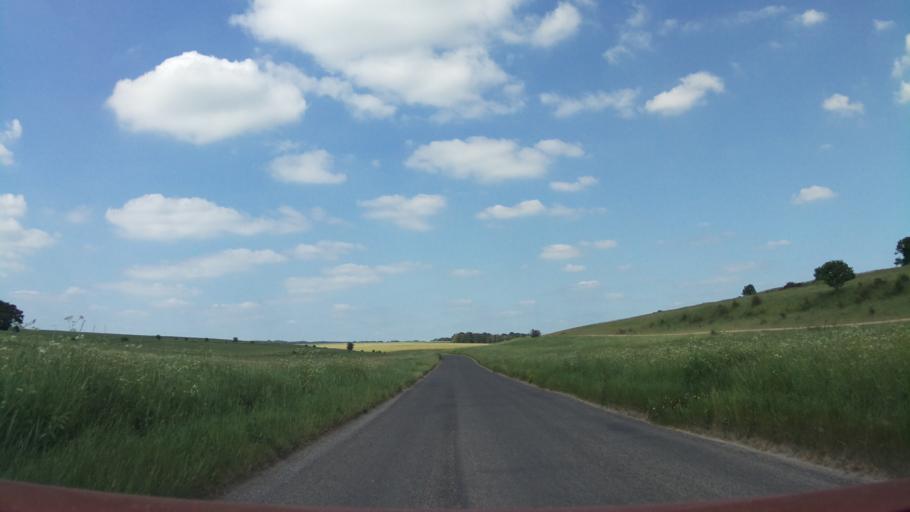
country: GB
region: England
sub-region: Wiltshire
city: Milston
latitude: 51.2619
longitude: -1.7272
